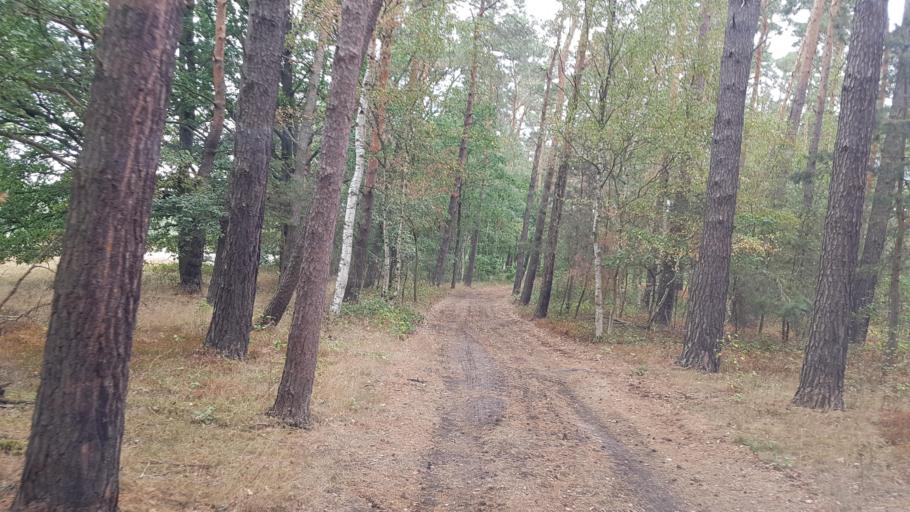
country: DE
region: Brandenburg
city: Sallgast
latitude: 51.6203
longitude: 13.8374
